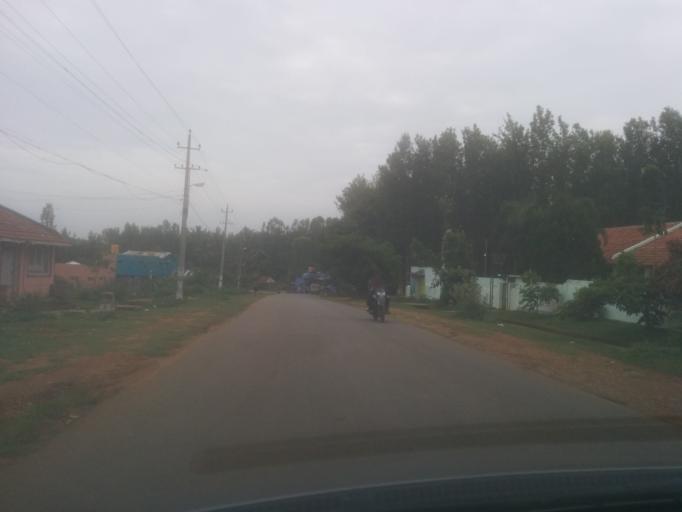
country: IN
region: Karnataka
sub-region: Chikmagalur
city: Chikmagalur
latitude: 13.3548
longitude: 75.7594
